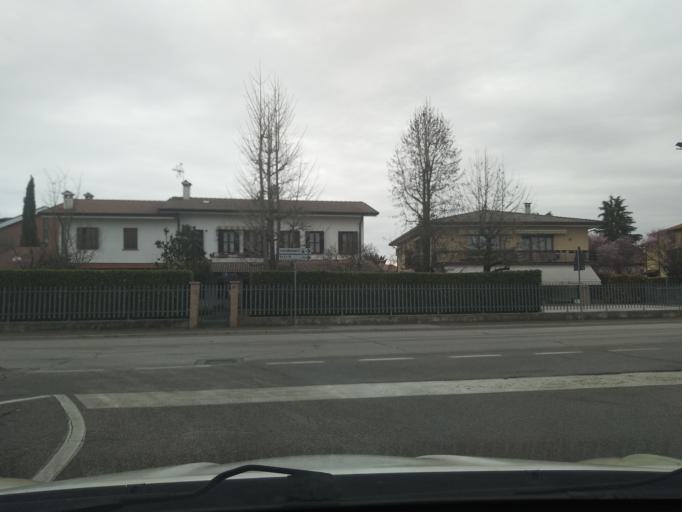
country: IT
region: Veneto
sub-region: Provincia di Padova
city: Selvazzano Dentro
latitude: 45.3896
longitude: 11.7859
